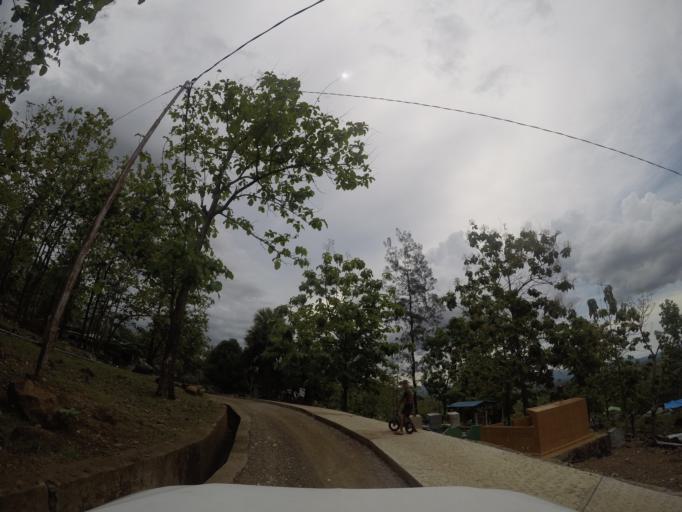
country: TL
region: Bobonaro
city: Maliana
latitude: -8.9958
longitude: 125.2146
